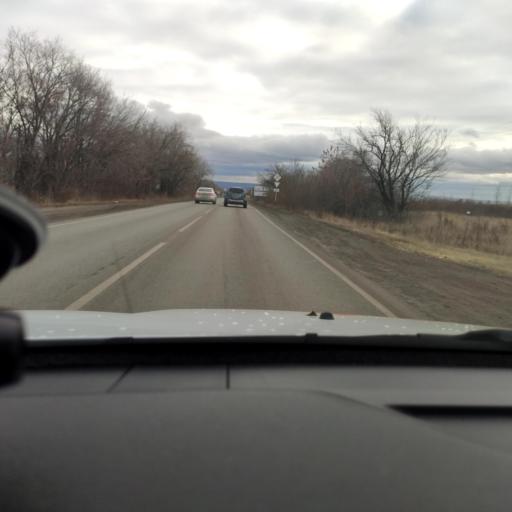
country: RU
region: Samara
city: Petra-Dubrava
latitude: 53.2890
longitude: 50.3726
